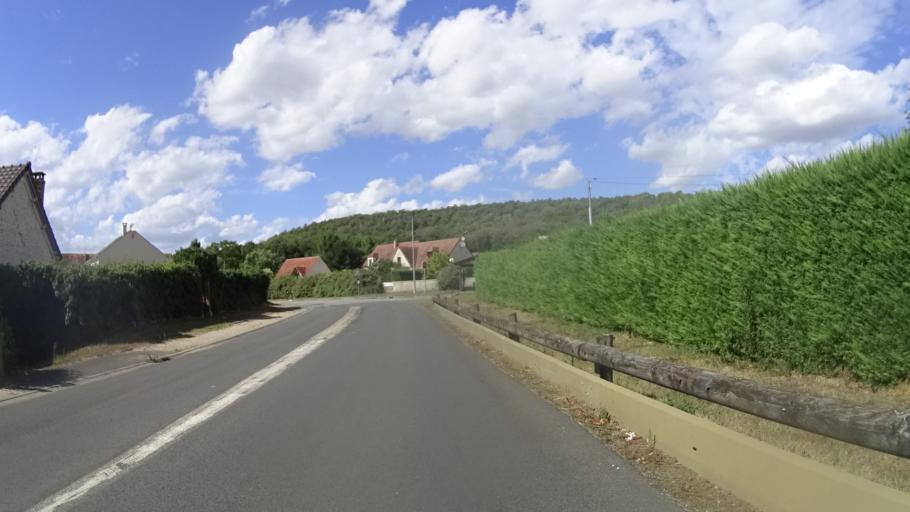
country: FR
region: Ile-de-France
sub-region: Departement de l'Essonne
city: Boutigny-sur-Essonne
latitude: 48.4529
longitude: 2.3646
